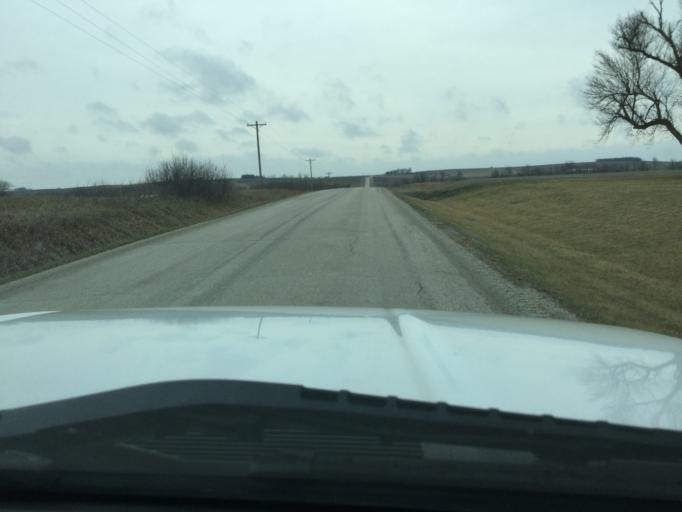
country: US
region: Kansas
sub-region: Nemaha County
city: Sabetha
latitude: 39.8852
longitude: -95.7139
